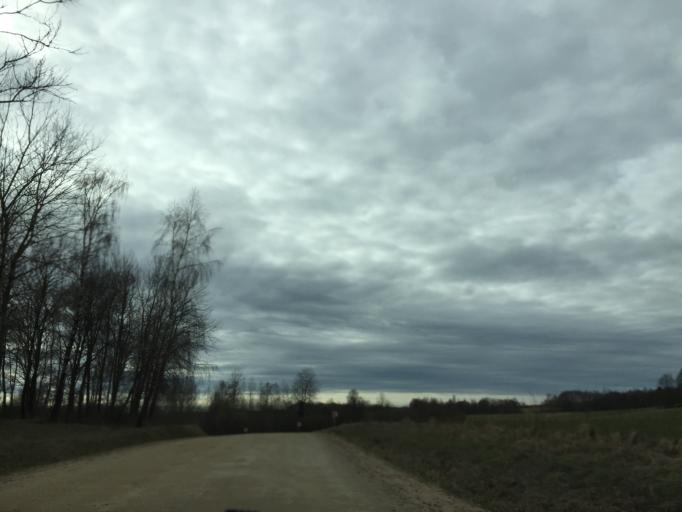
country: LT
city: Silale
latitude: 55.6118
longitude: 22.1802
